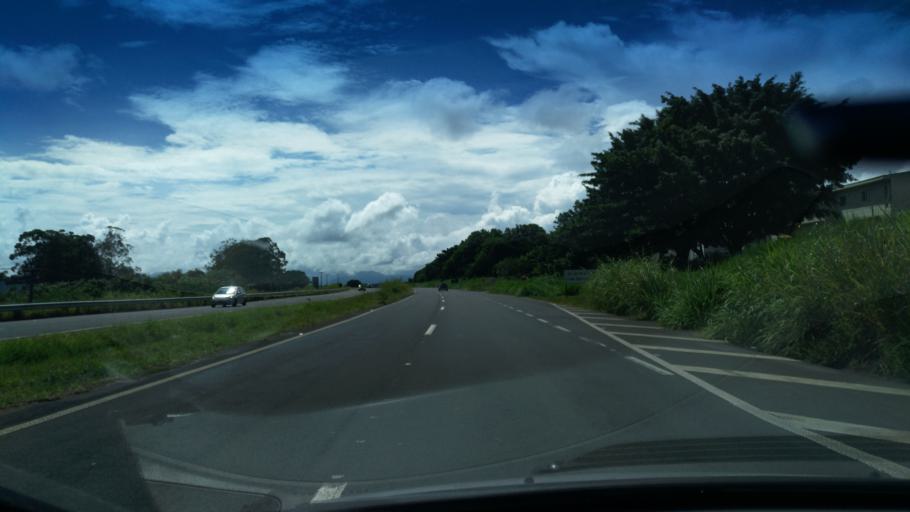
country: BR
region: Sao Paulo
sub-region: Santo Antonio Do Jardim
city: Espirito Santo do Pinhal
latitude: -22.1780
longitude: -46.7516
